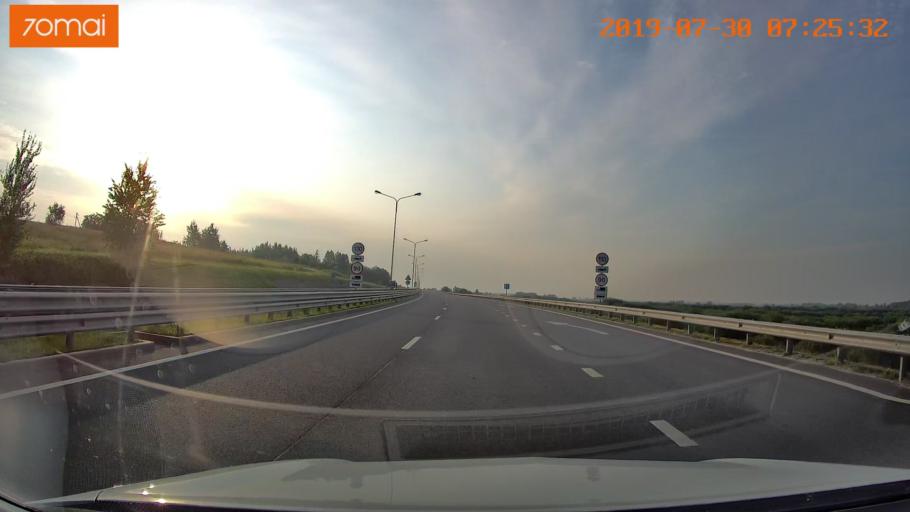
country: RU
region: Kaliningrad
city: Gvardeysk
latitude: 54.6862
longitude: 20.8370
